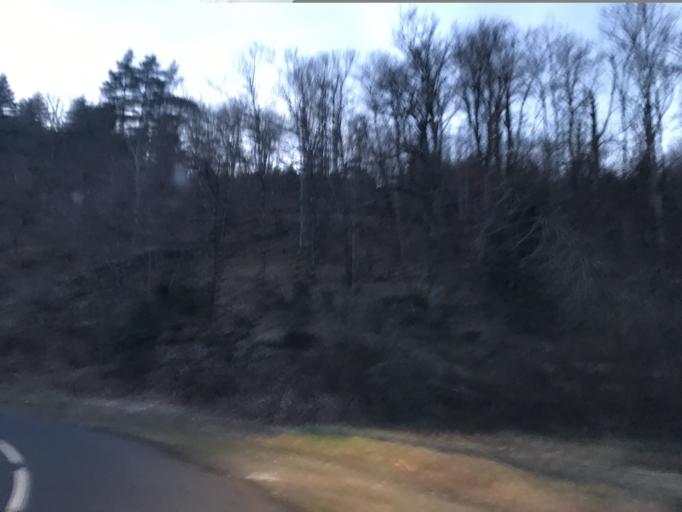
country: FR
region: Auvergne
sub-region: Departement du Puy-de-Dome
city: Thiers
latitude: 45.8670
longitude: 3.5629
